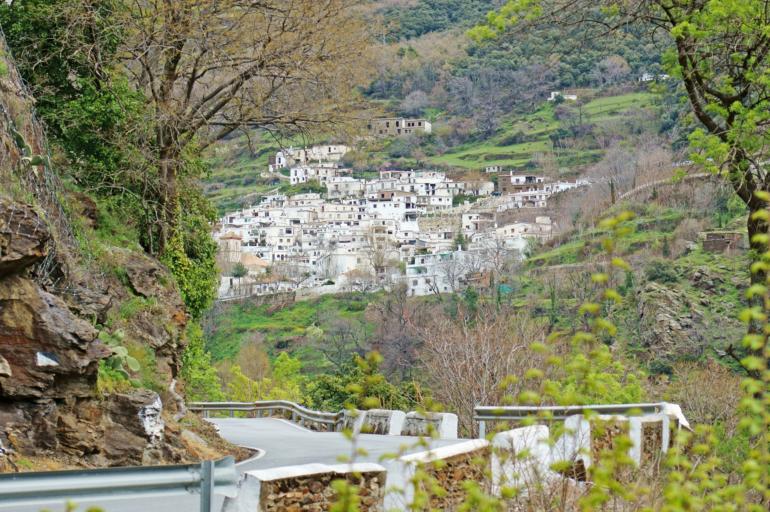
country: ES
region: Andalusia
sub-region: Provincia de Granada
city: Pampaneira
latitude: 36.9396
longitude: -3.3601
